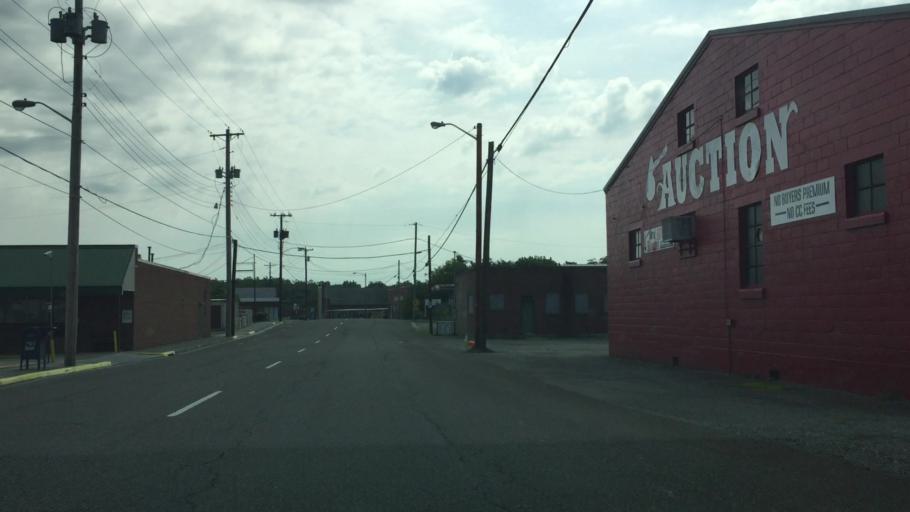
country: US
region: Virginia
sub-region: Pulaski County
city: Pulaski
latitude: 37.0477
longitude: -80.7769
